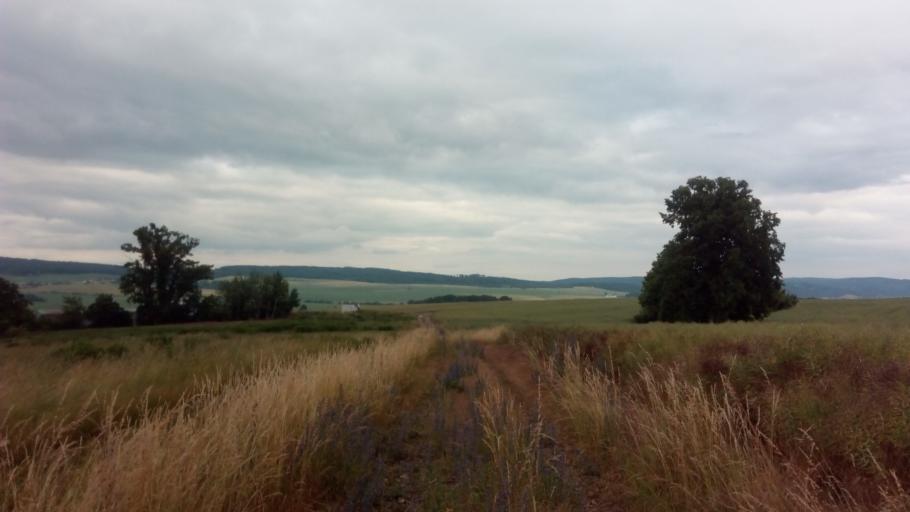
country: CZ
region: South Moravian
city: Ricany
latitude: 49.2106
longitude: 16.3866
